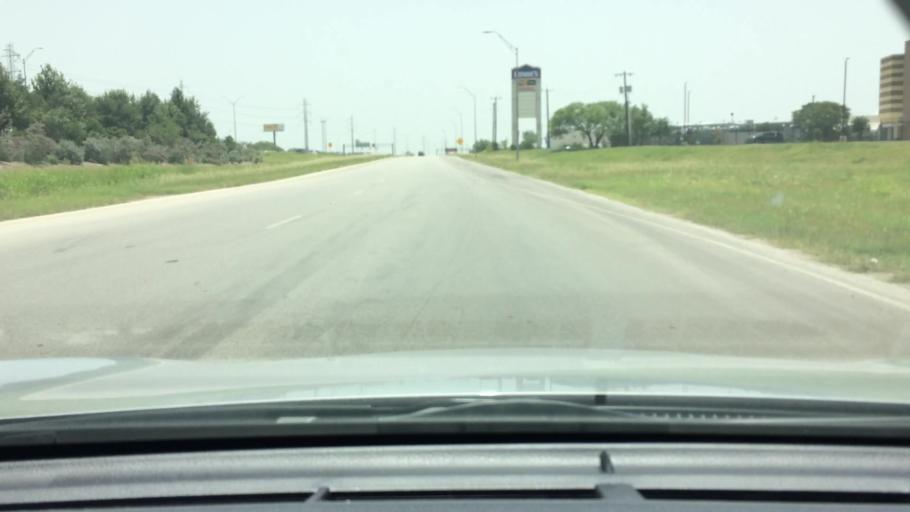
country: US
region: Texas
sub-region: Bexar County
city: China Grove
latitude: 29.3516
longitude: -98.4284
